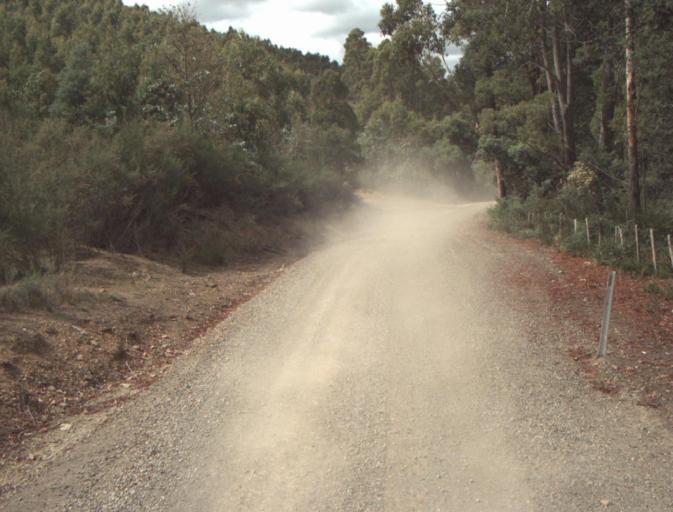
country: AU
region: Tasmania
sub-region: Northern Midlands
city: Evandale
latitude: -41.4510
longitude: 147.4806
